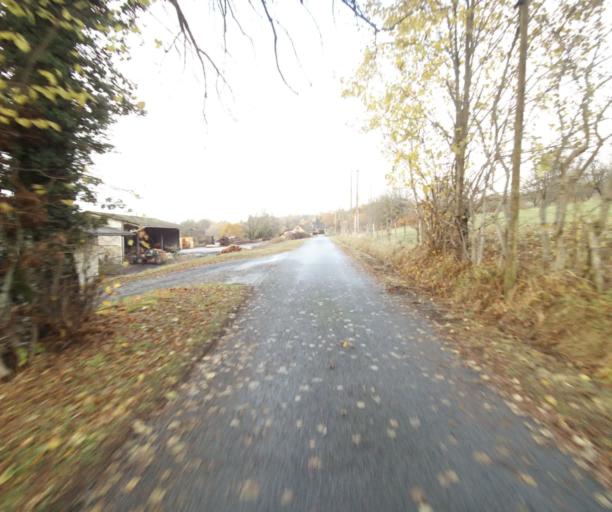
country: FR
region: Limousin
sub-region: Departement de la Correze
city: Cornil
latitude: 45.2194
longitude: 1.6613
